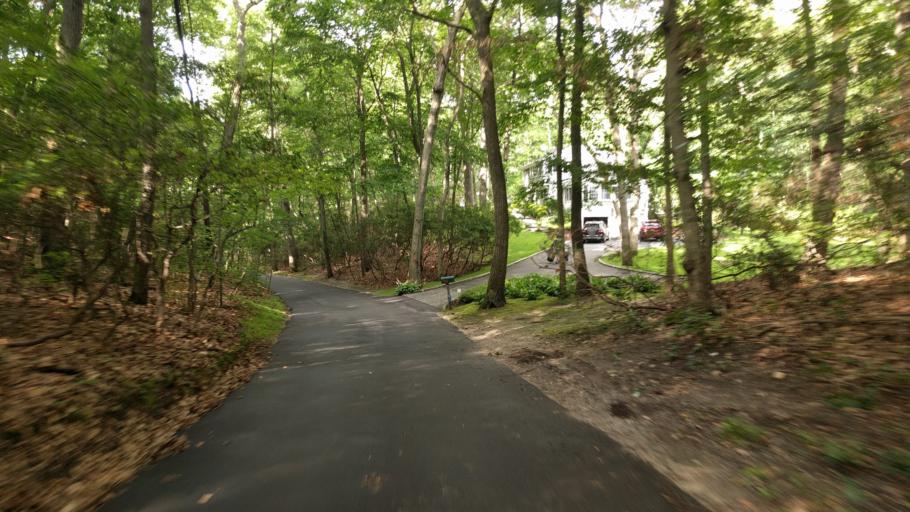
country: US
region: New York
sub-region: Nassau County
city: Oyster Bay Cove
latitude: 40.8750
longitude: -73.4923
